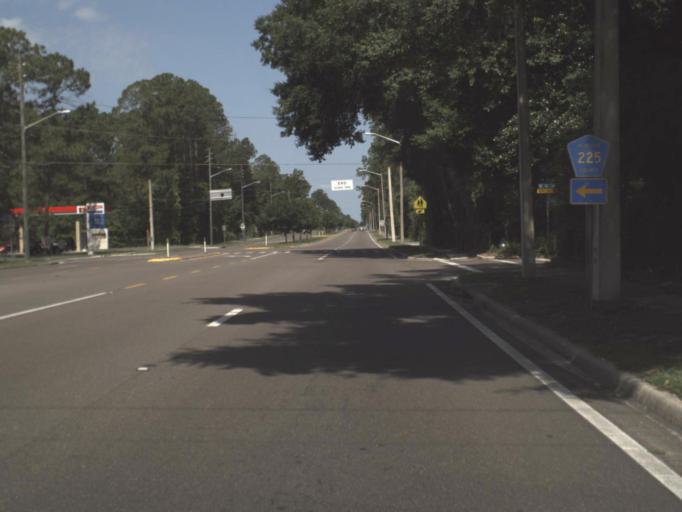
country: US
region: Florida
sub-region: Alachua County
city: Gainesville
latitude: 29.6519
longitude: -82.2716
